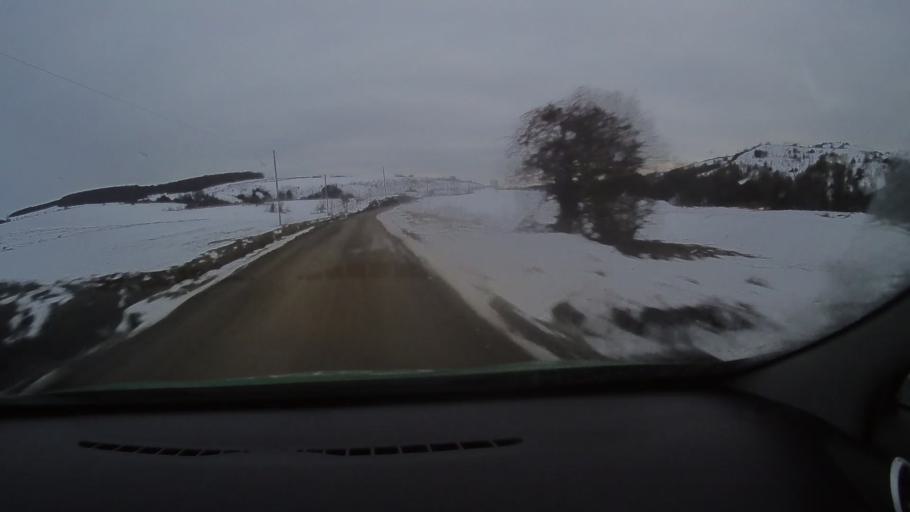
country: RO
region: Harghita
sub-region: Comuna Darjiu
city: Darjiu
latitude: 46.2070
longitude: 25.2433
